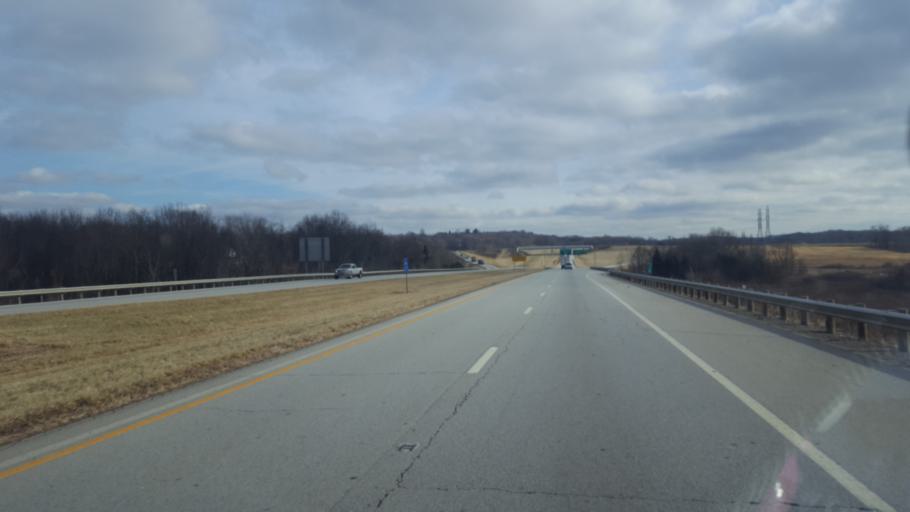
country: US
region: Ohio
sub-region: Stark County
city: East Canton
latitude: 40.7837
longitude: -81.3292
